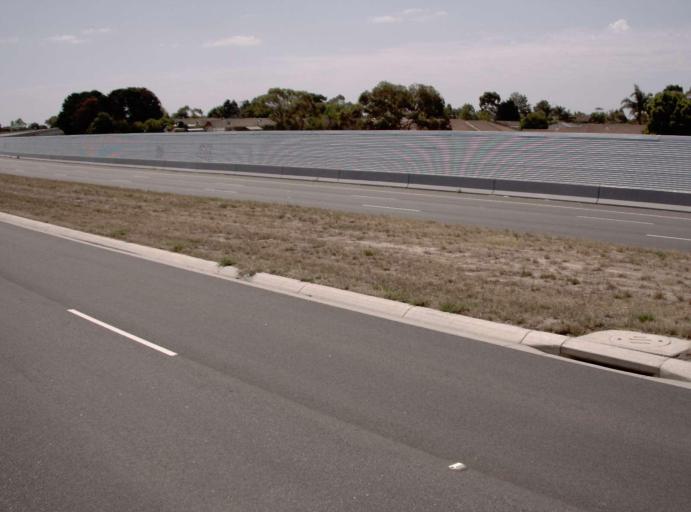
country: AU
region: Victoria
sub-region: Greater Dandenong
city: Keysborough
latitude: -37.9968
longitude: 145.1597
